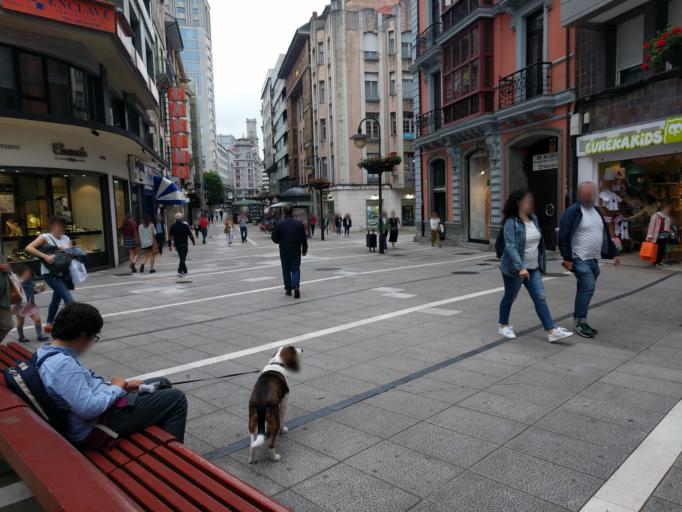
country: ES
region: Asturias
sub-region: Province of Asturias
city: Oviedo
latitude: 43.3645
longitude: -5.8498
